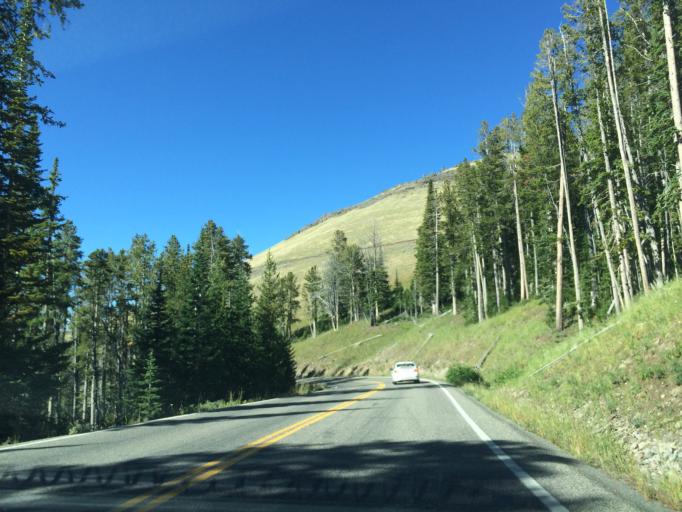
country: US
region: Montana
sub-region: Gallatin County
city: West Yellowstone
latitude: 44.8125
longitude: -110.4457
